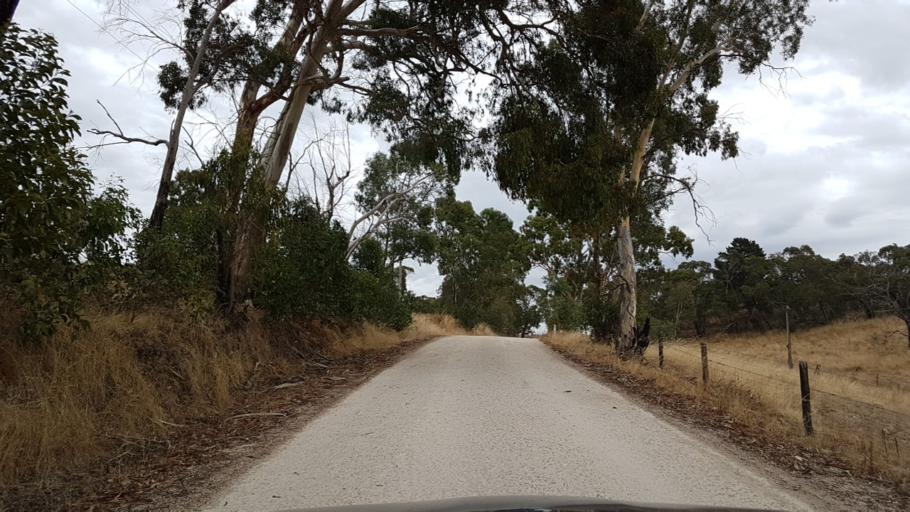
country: AU
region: South Australia
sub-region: Tea Tree Gully
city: Golden Grove
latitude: -34.8037
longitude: 138.8081
